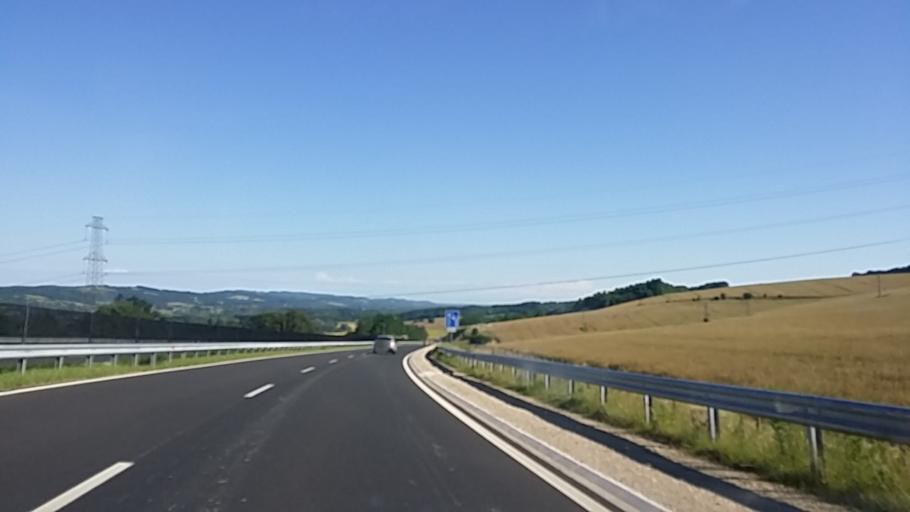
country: HU
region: Zala
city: Heviz
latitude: 46.7898
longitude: 17.1315
